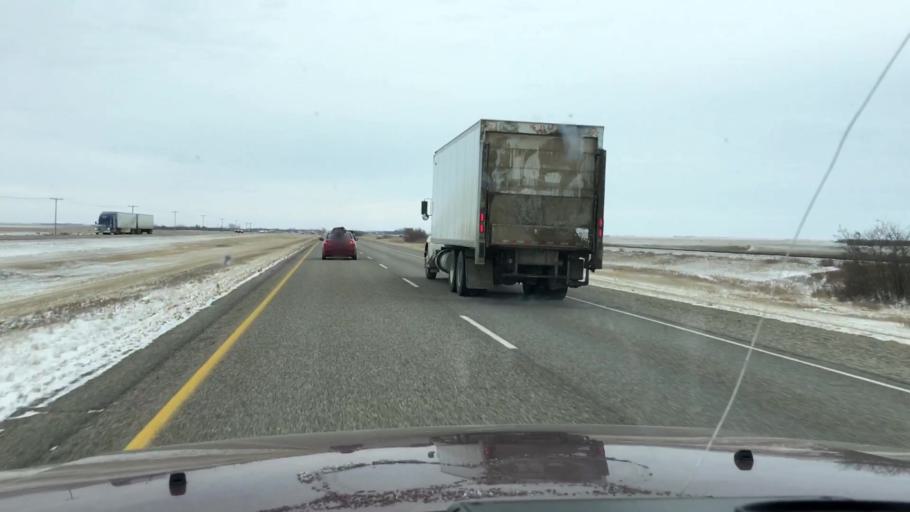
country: CA
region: Saskatchewan
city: Watrous
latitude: 51.1789
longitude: -105.9379
